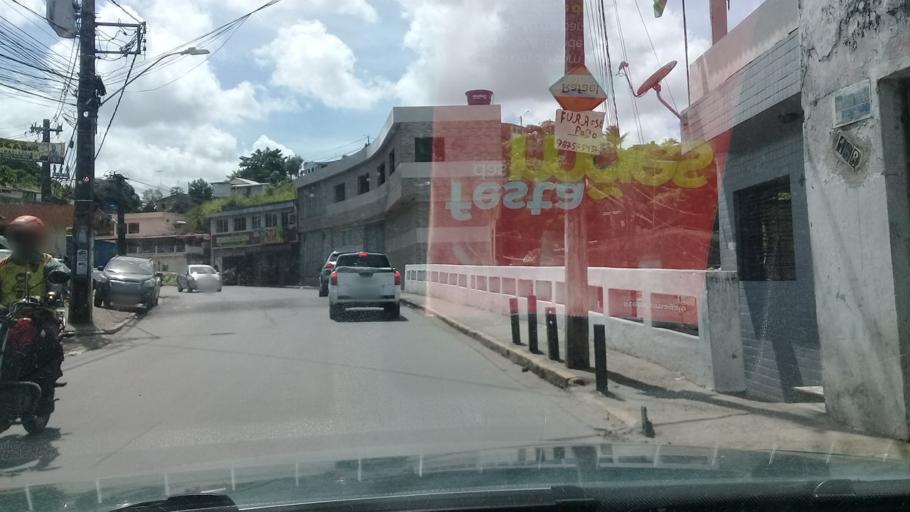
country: BR
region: Pernambuco
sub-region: Jaboatao Dos Guararapes
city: Jaboatao dos Guararapes
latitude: -8.1098
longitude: -35.0159
